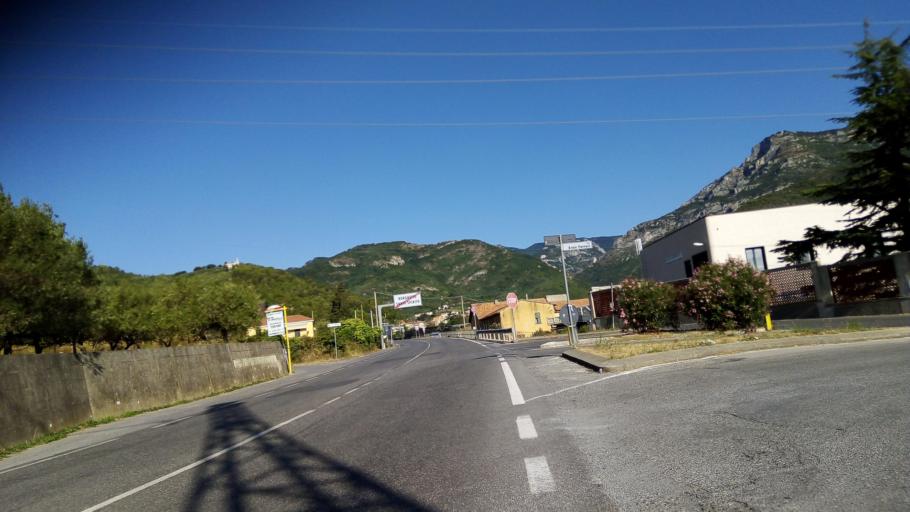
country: IT
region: Liguria
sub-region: Provincia di Savona
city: Toirano
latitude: 44.1206
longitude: 8.2202
